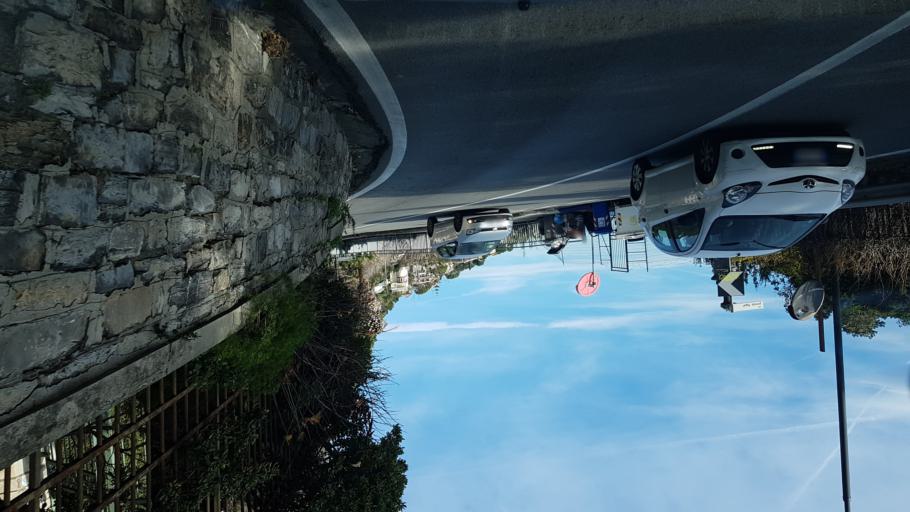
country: IT
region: Liguria
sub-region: Provincia di Genova
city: Recco
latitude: 44.3635
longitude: 9.1259
